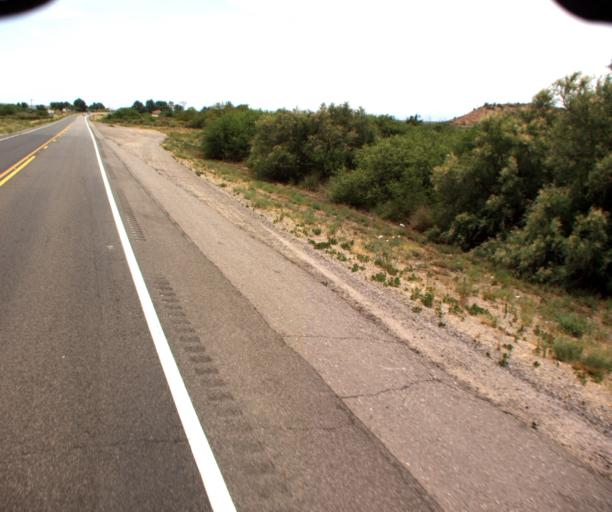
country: US
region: Arizona
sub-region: Graham County
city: Bylas
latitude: 33.1532
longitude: -110.1285
